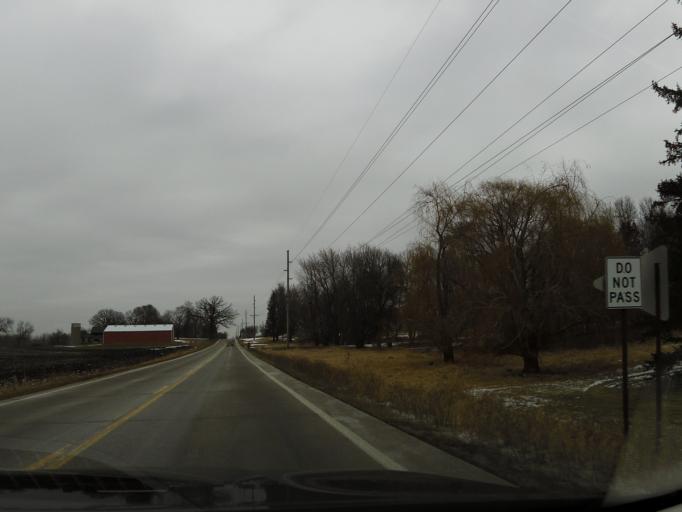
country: US
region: Minnesota
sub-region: Hennepin County
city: Independence
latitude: 44.9926
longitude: -93.7272
